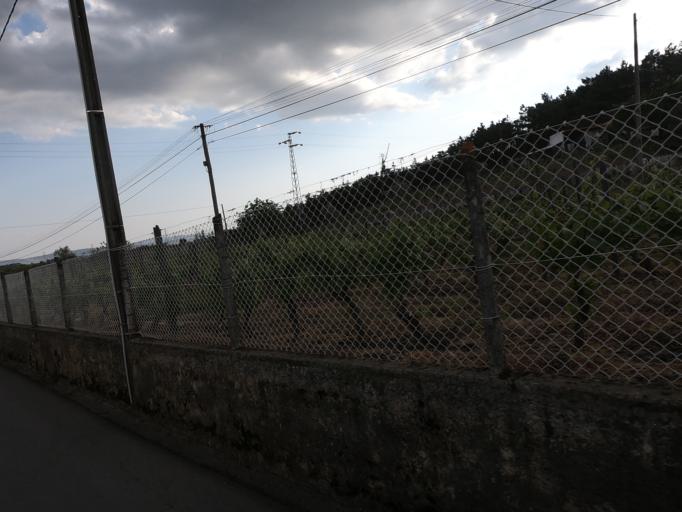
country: PT
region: Vila Real
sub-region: Sabrosa
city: Vilela
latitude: 41.2152
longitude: -7.6691
